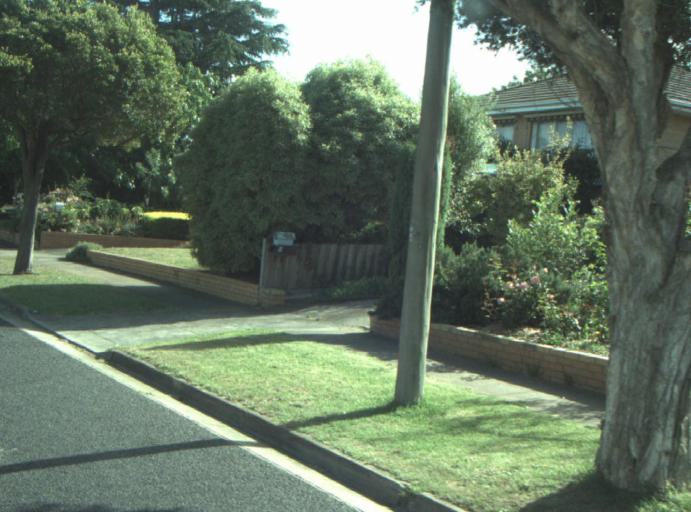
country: AU
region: Victoria
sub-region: Greater Geelong
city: Wandana Heights
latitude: -38.1771
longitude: 144.3250
